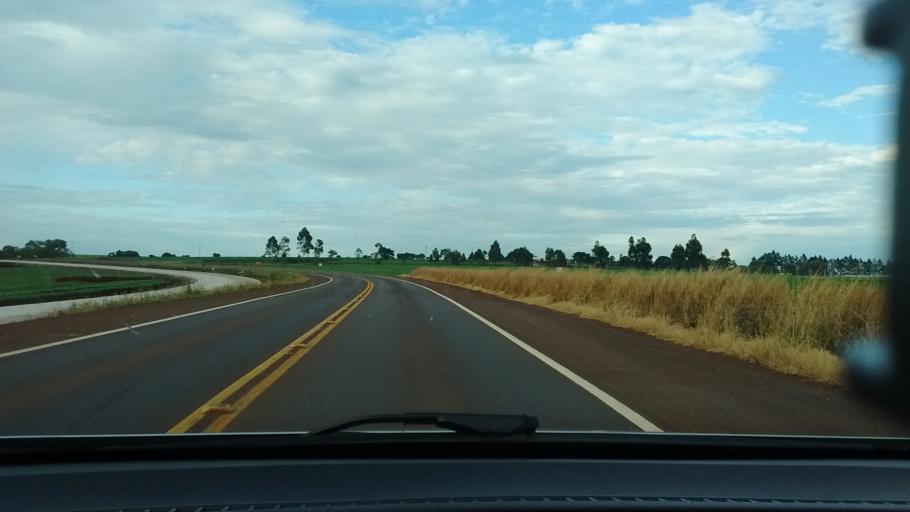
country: BR
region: Parana
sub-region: Cascavel
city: Cascavel
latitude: -25.0375
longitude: -53.5552
